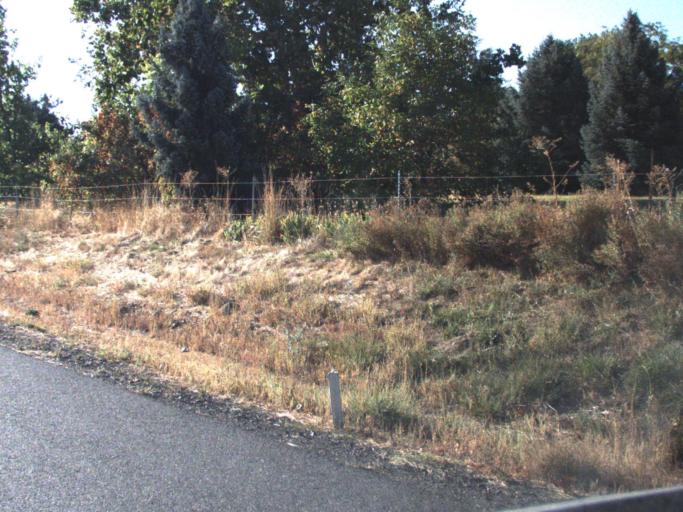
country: US
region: Washington
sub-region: Benton County
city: West Richland
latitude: 46.2969
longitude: -119.3254
